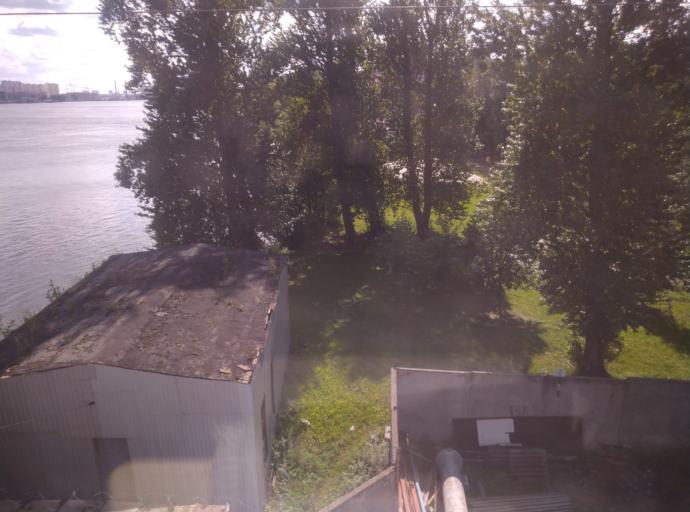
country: RU
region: St.-Petersburg
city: Centralniy
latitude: 59.9142
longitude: 30.4058
